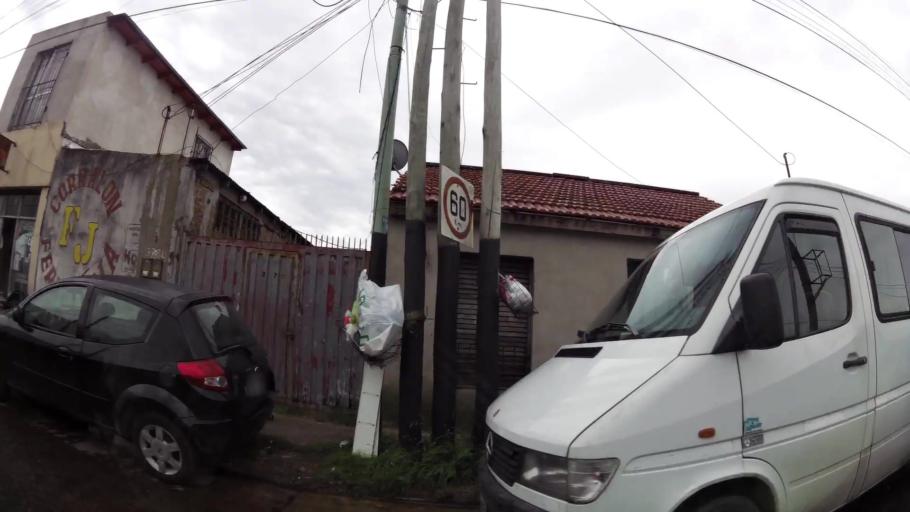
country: AR
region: Buenos Aires
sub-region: Partido de Quilmes
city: Quilmes
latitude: -34.7609
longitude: -58.2258
